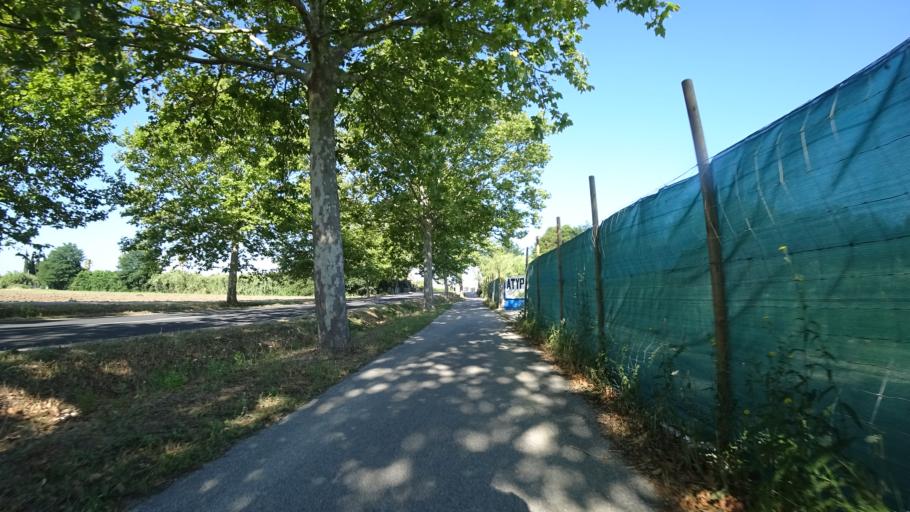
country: FR
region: Languedoc-Roussillon
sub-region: Departement des Pyrenees-Orientales
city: Villelongue-de-la-Salanque
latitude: 42.7274
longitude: 2.9940
